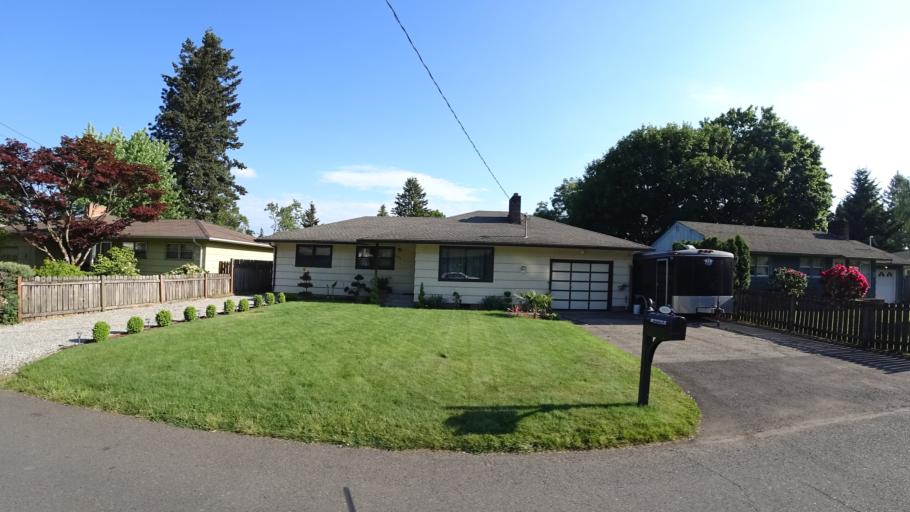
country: US
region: Oregon
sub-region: Multnomah County
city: Fairview
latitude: 45.5150
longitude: -122.4982
